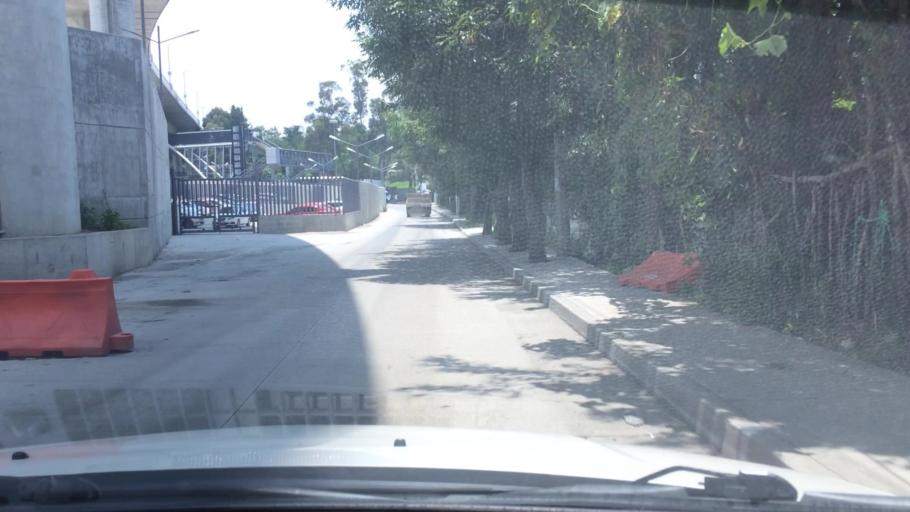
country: MX
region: Mexico City
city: Xochimilco
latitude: 19.2431
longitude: -99.1483
